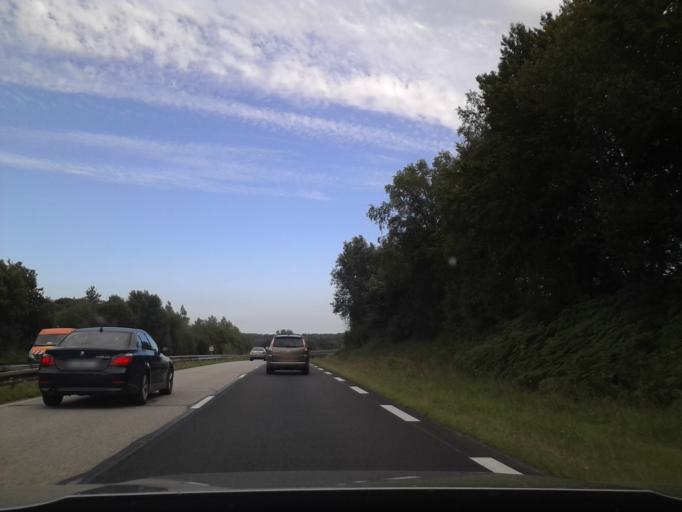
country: FR
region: Lower Normandy
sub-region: Departement de la Manche
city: Brix
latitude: 49.5669
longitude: -1.5716
